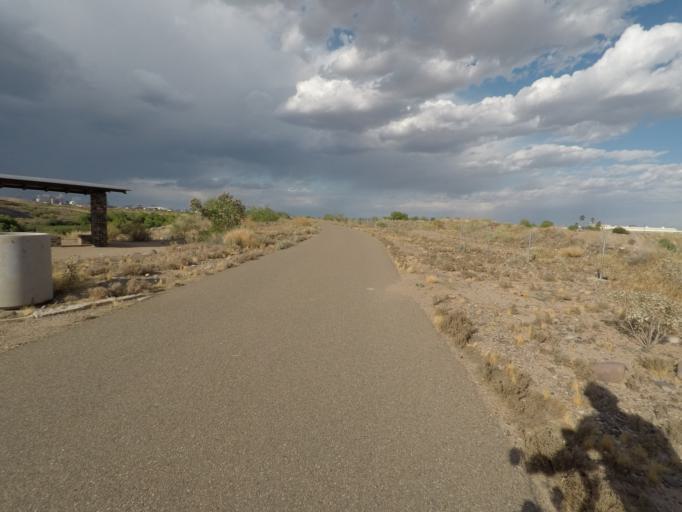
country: US
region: Arizona
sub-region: Maricopa County
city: Phoenix
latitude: 33.4142
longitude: -112.0884
